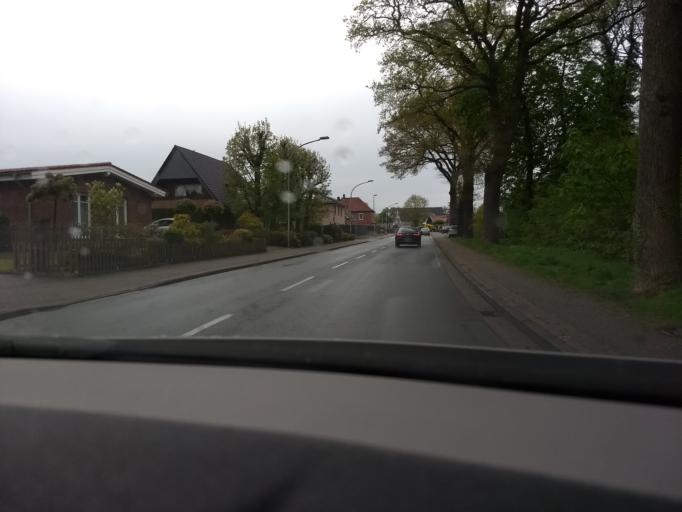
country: DE
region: Lower Saxony
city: Rastede
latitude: 53.2032
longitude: 8.2445
